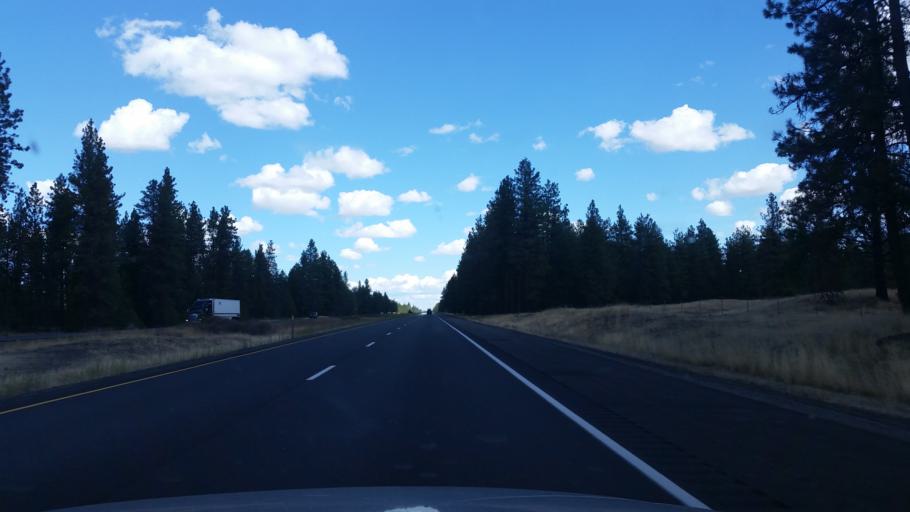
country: US
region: Washington
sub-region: Spokane County
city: Medical Lake
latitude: 47.4771
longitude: -117.7304
